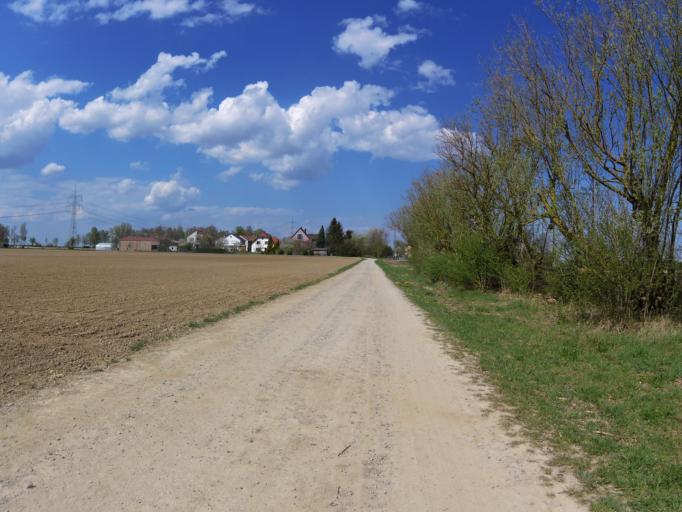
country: DE
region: Bavaria
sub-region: Regierungsbezirk Unterfranken
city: Oberpleichfeld
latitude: 49.8509
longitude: 10.1029
